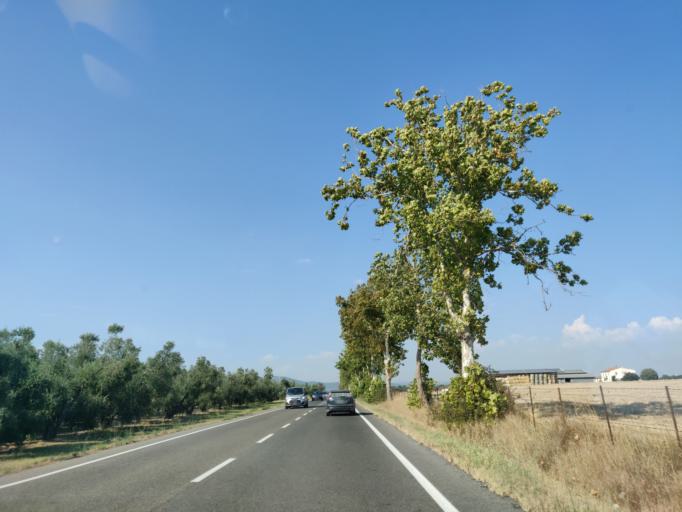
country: IT
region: Latium
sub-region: Provincia di Viterbo
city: Montalto di Castro
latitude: 42.3833
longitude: 11.6600
